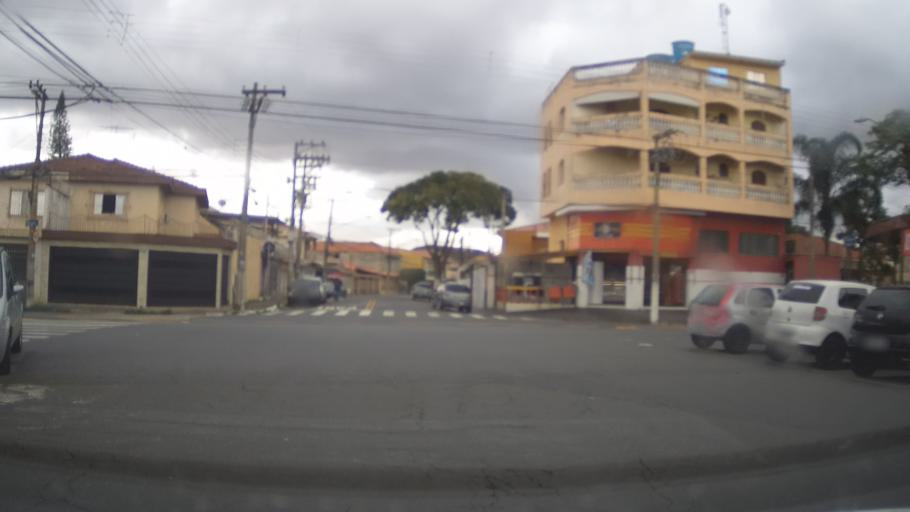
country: BR
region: Sao Paulo
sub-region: Guarulhos
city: Guarulhos
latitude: -23.4651
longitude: -46.5583
